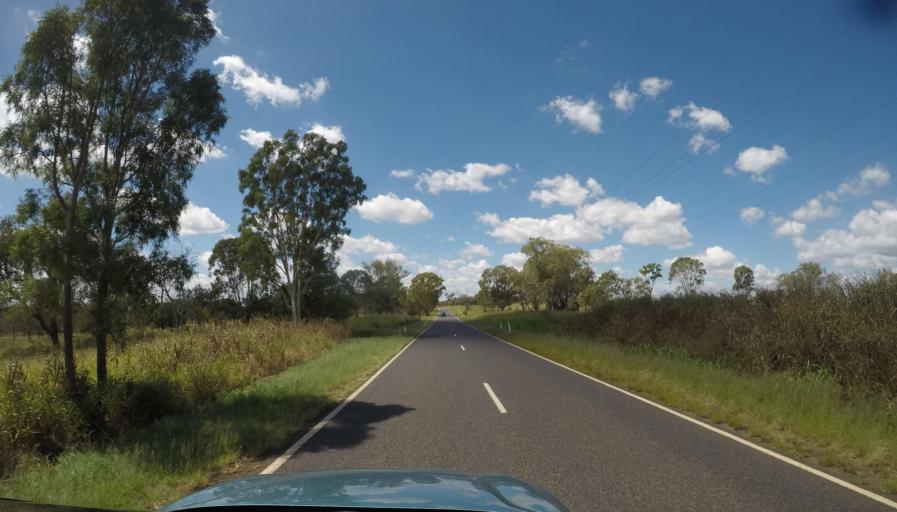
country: AU
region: Queensland
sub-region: Toowoomba
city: Oakey
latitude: -27.5547
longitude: 151.7009
